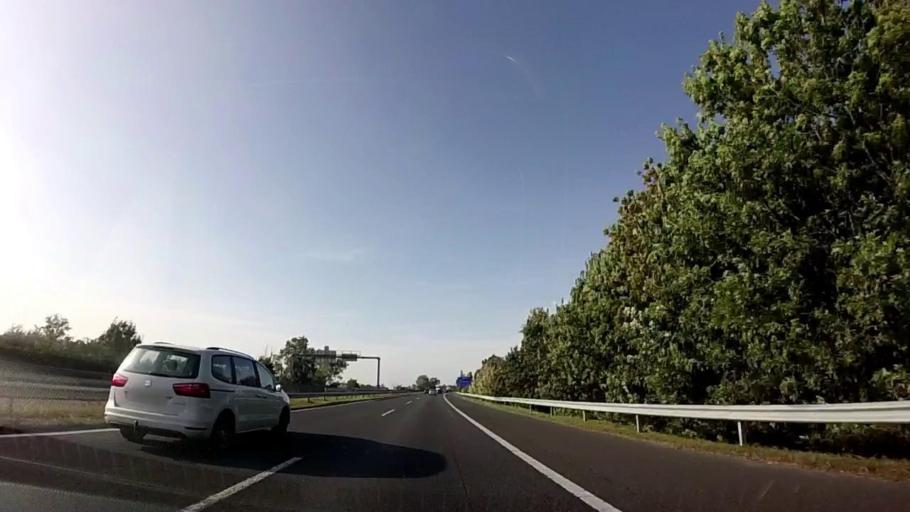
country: HU
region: Fejer
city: Kapolnasnyek
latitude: 47.2526
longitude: 18.6660
